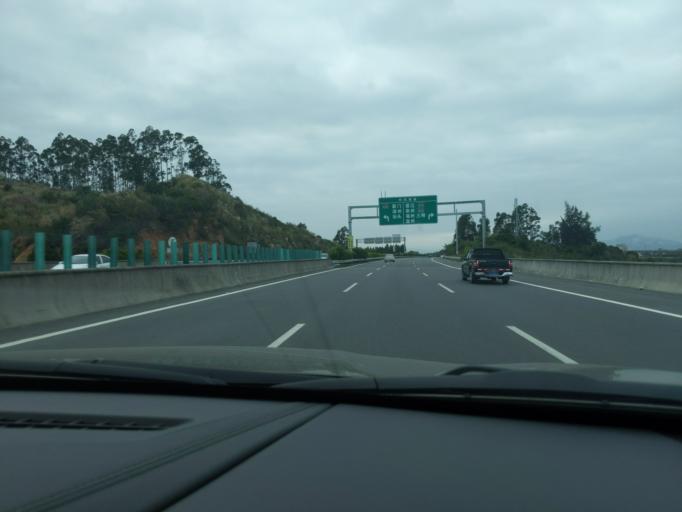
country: CN
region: Fujian
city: Neikeng
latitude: 24.7841
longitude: 118.4855
